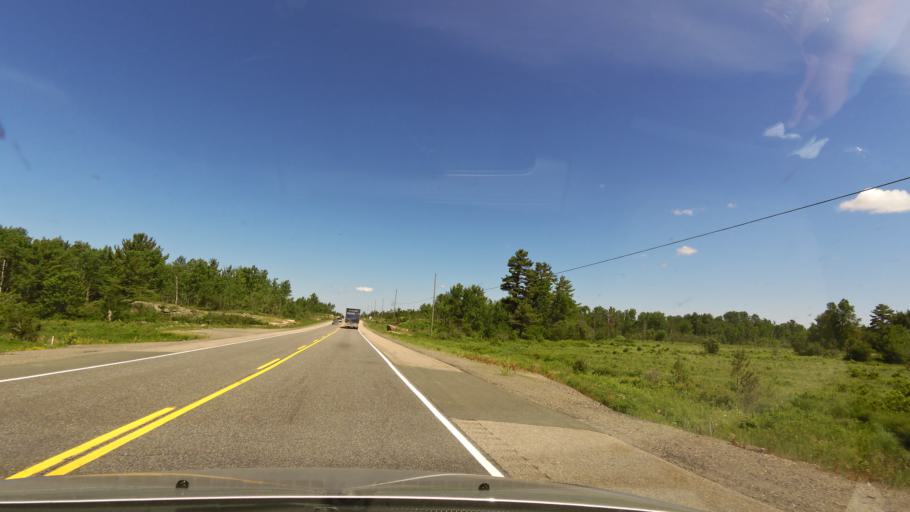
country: CA
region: Ontario
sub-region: Parry Sound District
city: Parry Sound
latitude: 45.7093
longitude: -80.4610
